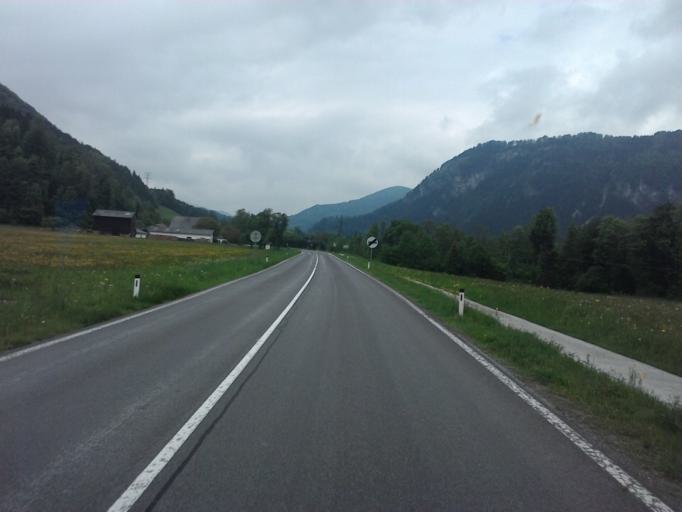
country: AT
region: Styria
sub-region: Politischer Bezirk Liezen
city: Gams bei Hieflau
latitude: 47.6464
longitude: 14.7539
